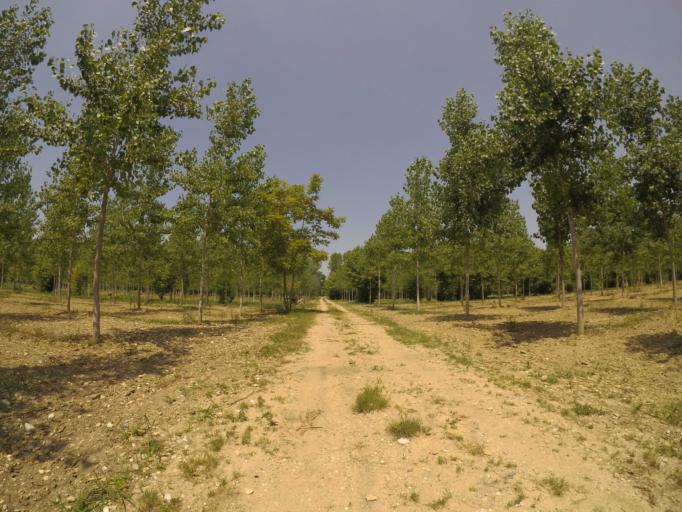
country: IT
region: Friuli Venezia Giulia
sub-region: Provincia di Udine
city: Bertiolo
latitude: 45.9122
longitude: 13.0398
